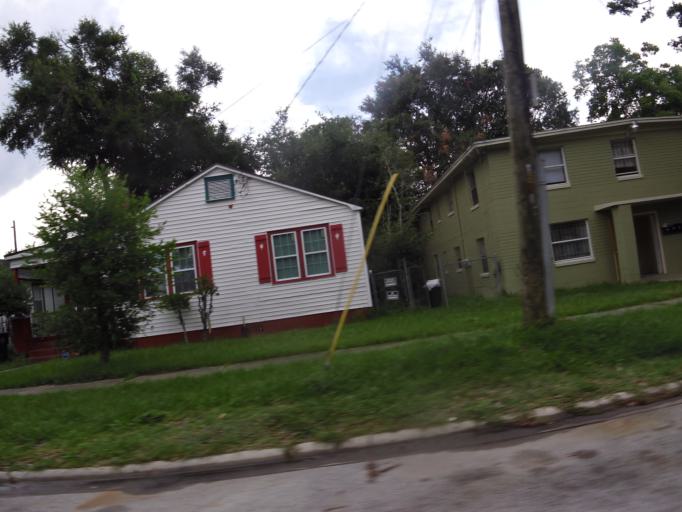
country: US
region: Florida
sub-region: Duval County
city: Jacksonville
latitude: 30.3465
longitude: -81.6737
